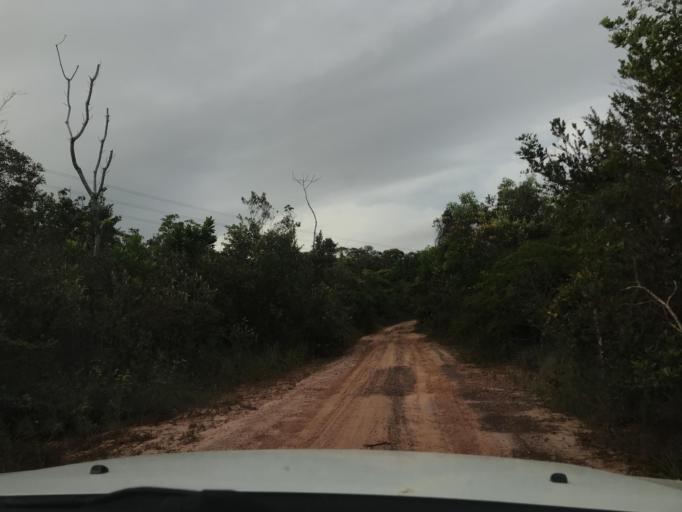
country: BR
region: Bahia
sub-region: Entre Rios
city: Entre Rios
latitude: -12.0522
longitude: -38.2279
